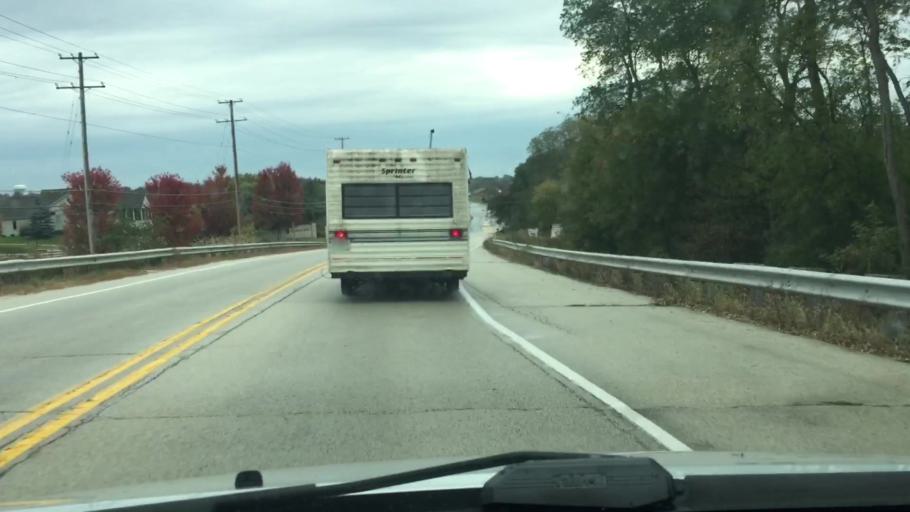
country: US
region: Wisconsin
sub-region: Waukesha County
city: Waukesha
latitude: 43.0221
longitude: -88.2952
